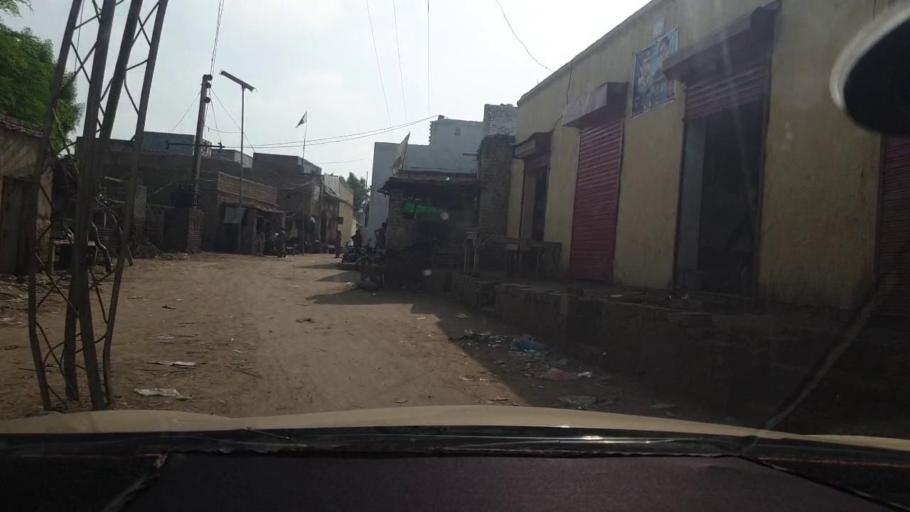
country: PK
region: Sindh
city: Goth Garelo
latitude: 27.4842
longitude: 68.0361
